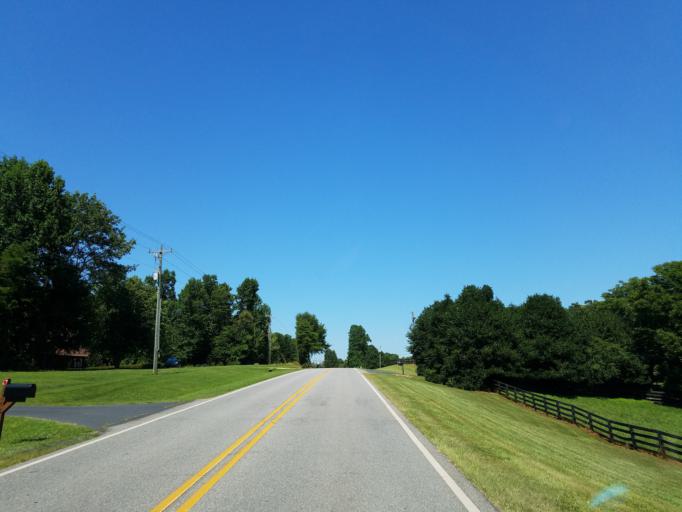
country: US
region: Georgia
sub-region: Dawson County
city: Dawsonville
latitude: 34.3342
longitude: -84.0444
